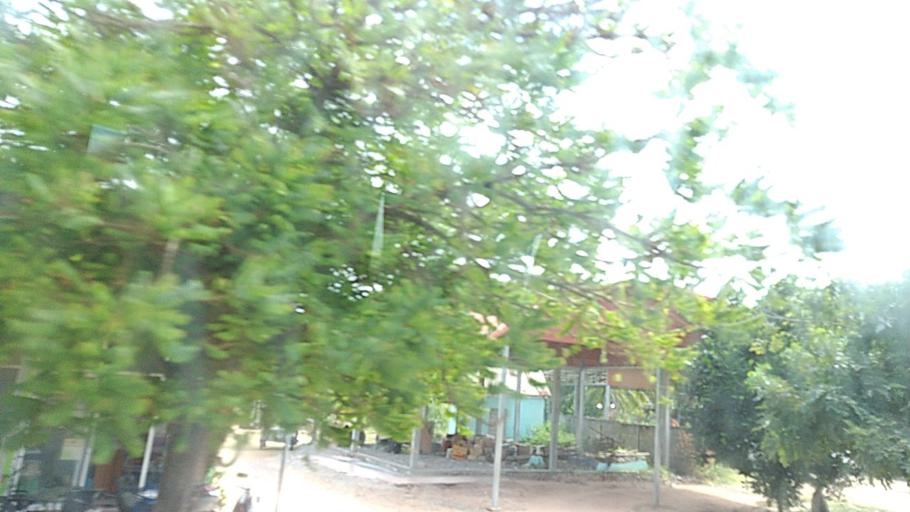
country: TH
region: Maha Sarakham
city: Chiang Yuen
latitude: 16.3872
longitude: 103.1021
